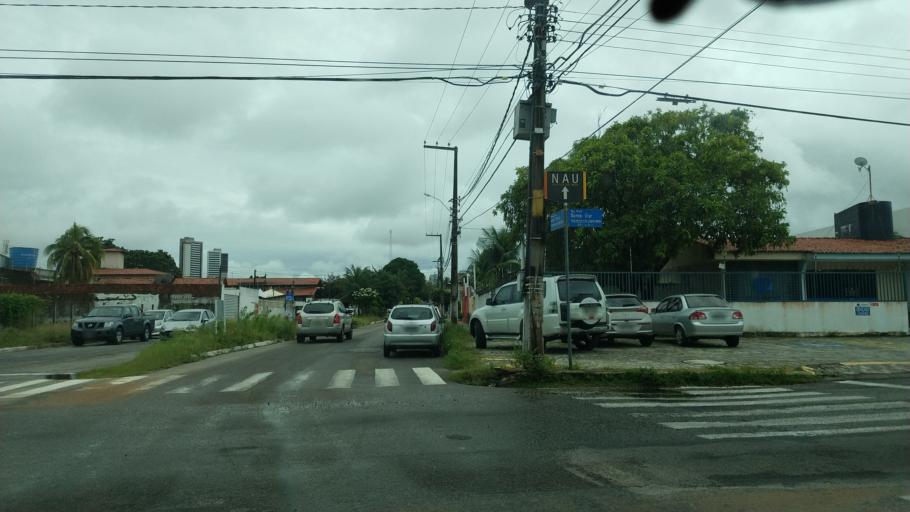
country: BR
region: Rio Grande do Norte
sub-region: Natal
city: Natal
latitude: -5.8518
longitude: -35.2021
